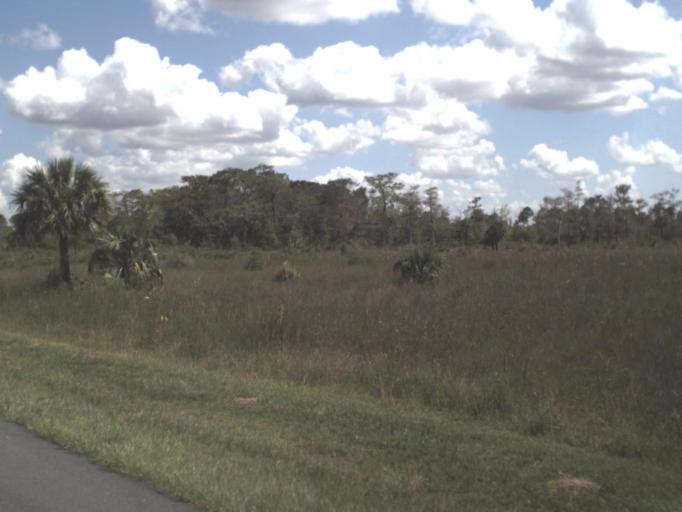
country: US
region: Florida
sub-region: Collier County
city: Lely Resort
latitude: 25.8664
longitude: -81.1276
